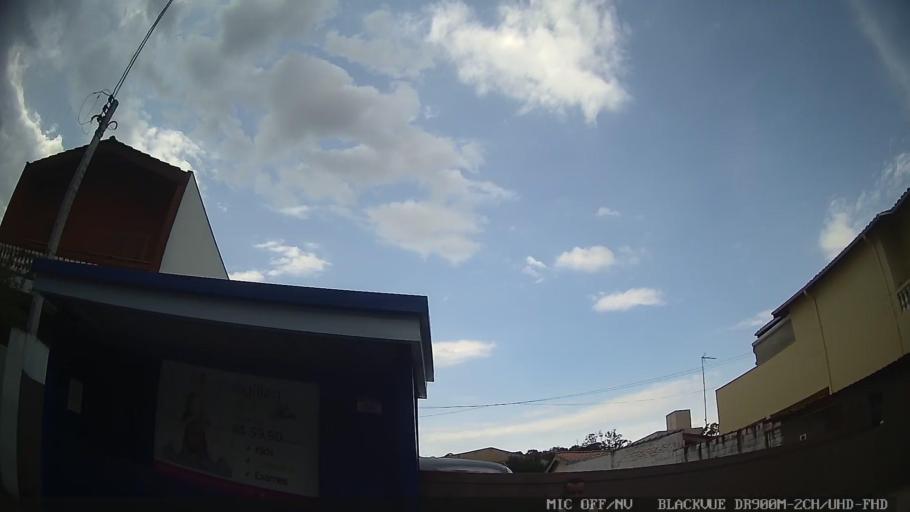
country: BR
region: Sao Paulo
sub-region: Itatiba
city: Itatiba
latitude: -23.0022
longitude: -46.8454
